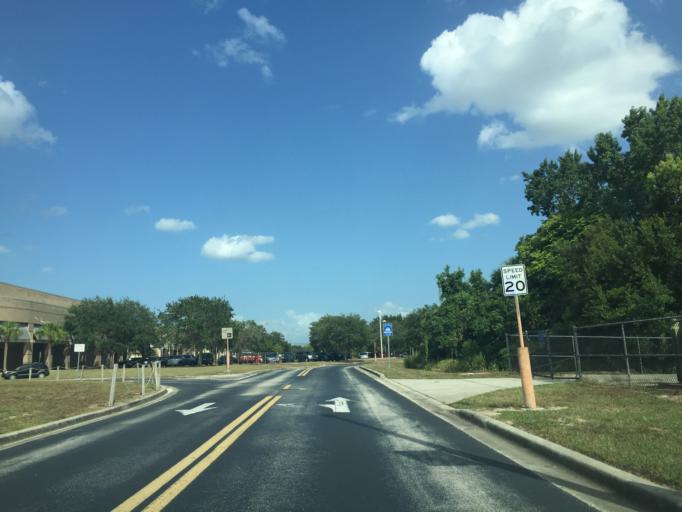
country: US
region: Florida
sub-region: Seminole County
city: Winter Springs
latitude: 28.7038
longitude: -81.2677
